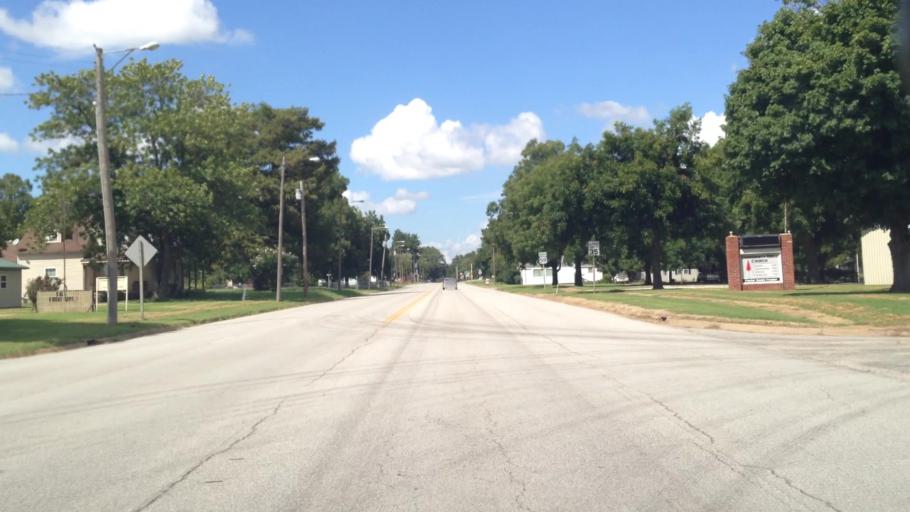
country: US
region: Kansas
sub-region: Labette County
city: Chetopa
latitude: 37.0328
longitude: -95.0859
